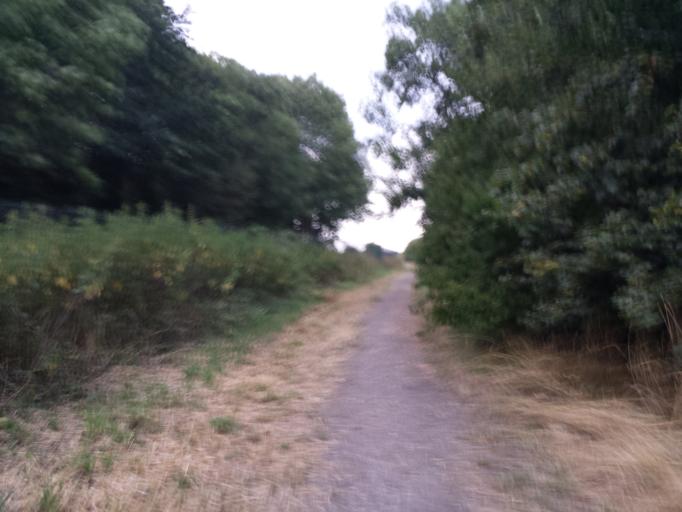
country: DE
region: Lower Saxony
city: Ritterhude
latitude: 53.1085
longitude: 8.7140
